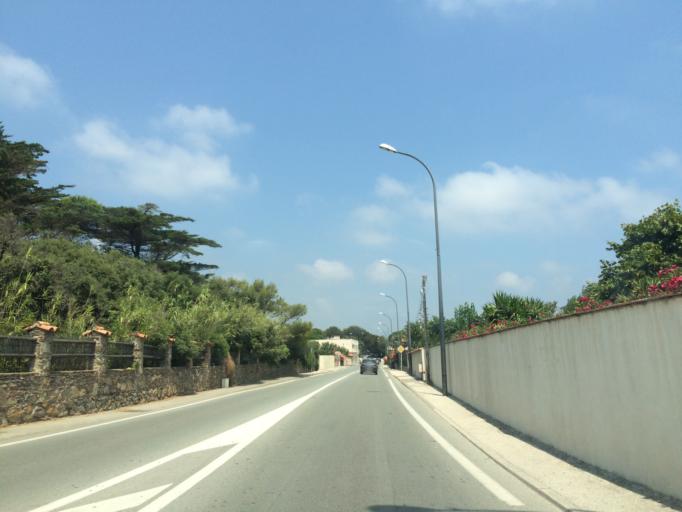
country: FR
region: Provence-Alpes-Cote d'Azur
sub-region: Departement du Var
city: Sainte-Maxime
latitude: 43.3234
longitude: 6.6639
